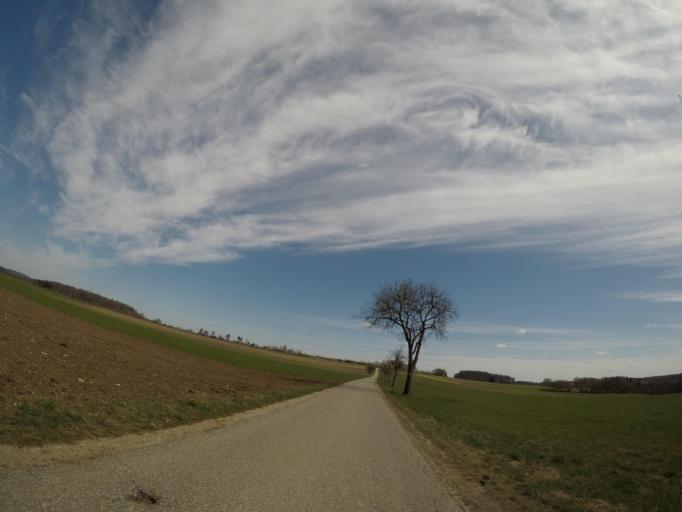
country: DE
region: Baden-Wuerttemberg
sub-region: Tuebingen Region
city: Mehrstetten
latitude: 48.3526
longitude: 9.6157
